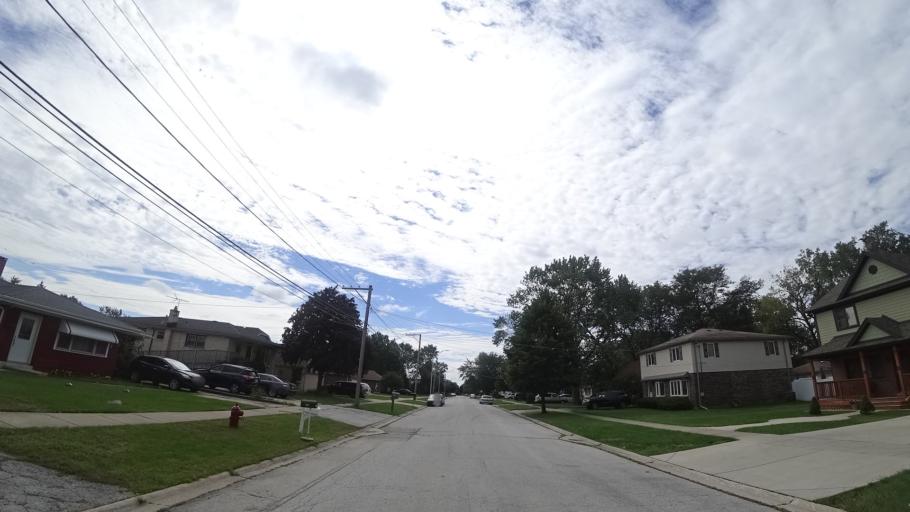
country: US
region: Illinois
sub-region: Cook County
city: Burbank
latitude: 41.7219
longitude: -87.7942
